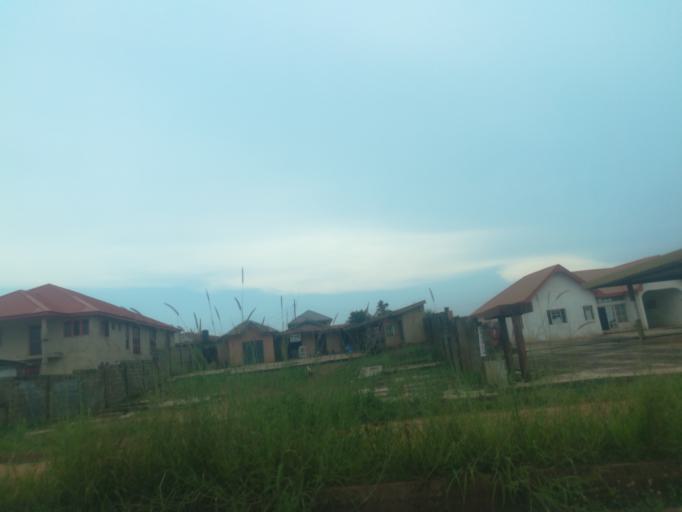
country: NG
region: Oyo
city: Ibadan
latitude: 7.3670
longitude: 3.8110
